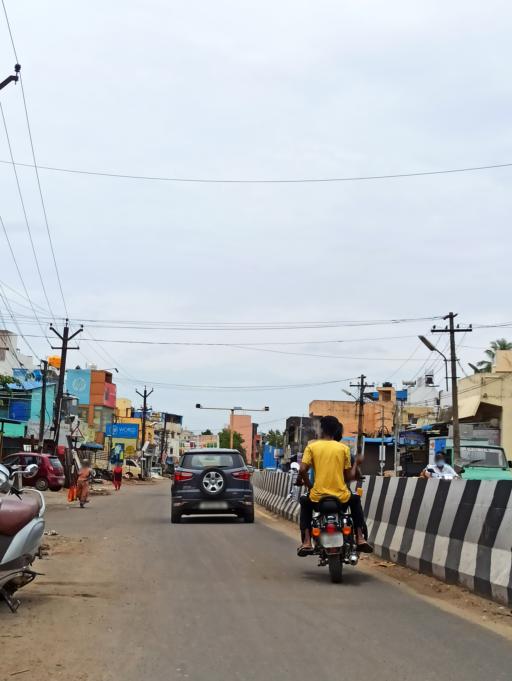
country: IN
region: Tamil Nadu
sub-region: Kancheepuram
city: Pallavaram
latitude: 12.9305
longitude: 80.1153
